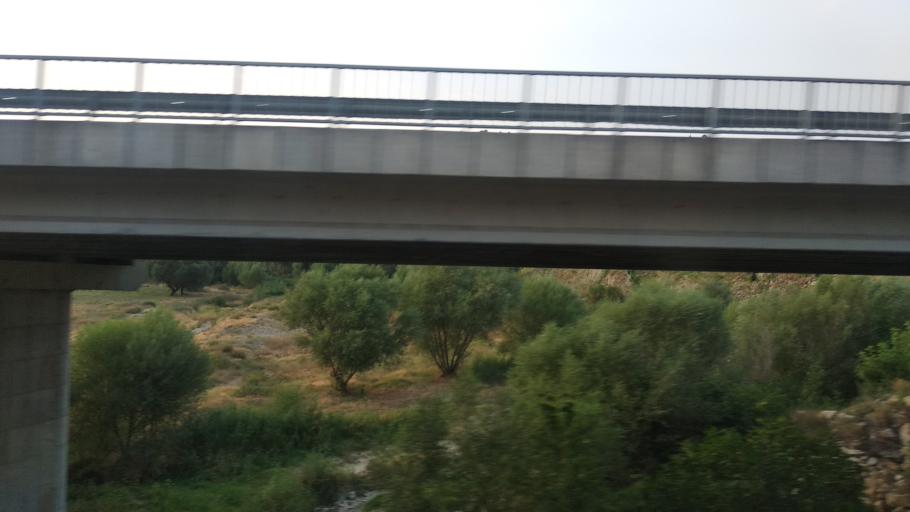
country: TR
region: Manisa
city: Selendi
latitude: 38.6016
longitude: 28.8147
